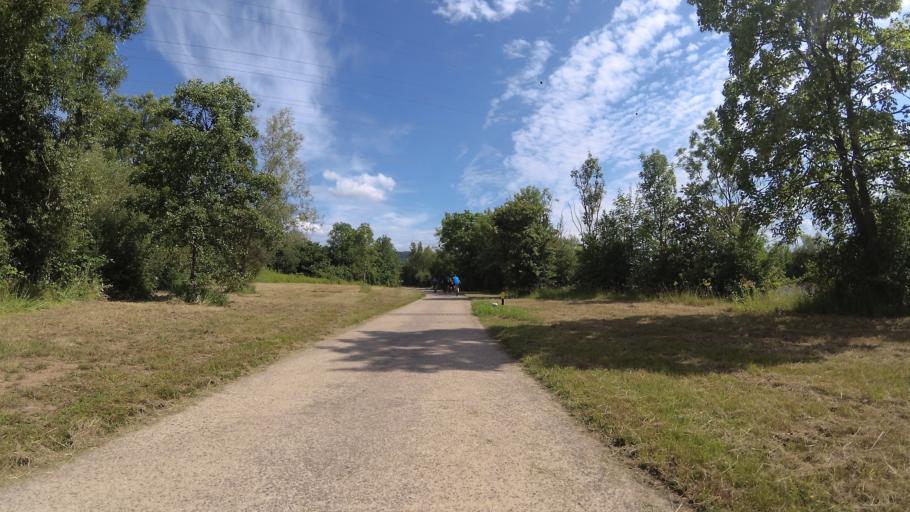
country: DE
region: Saarland
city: Merzig
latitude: 49.4535
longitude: 6.6289
